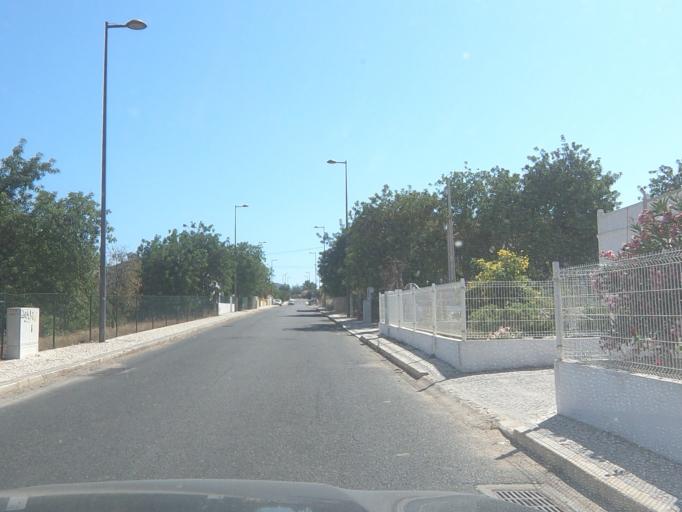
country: PT
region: Faro
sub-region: Faro
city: Santa Barbara de Nexe
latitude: 37.0889
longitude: -7.9882
